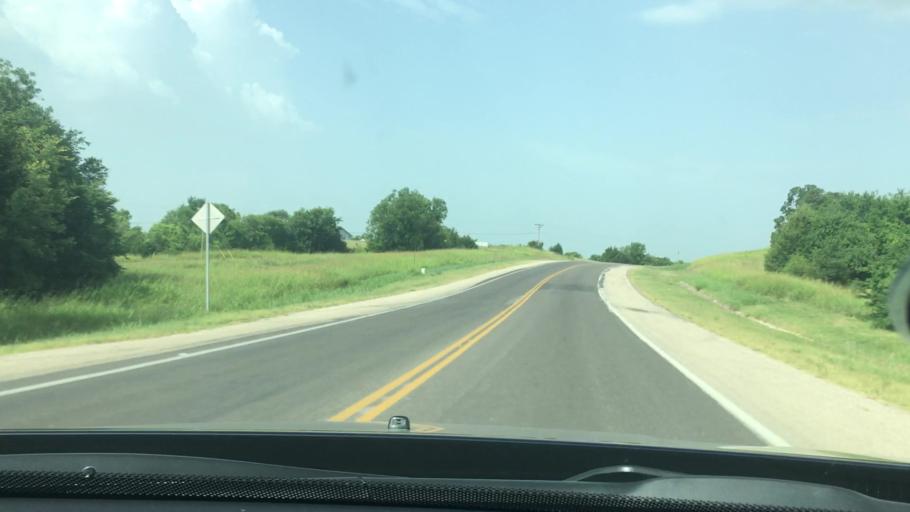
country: US
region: Oklahoma
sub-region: Pontotoc County
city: Ada
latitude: 34.7831
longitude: -96.7420
